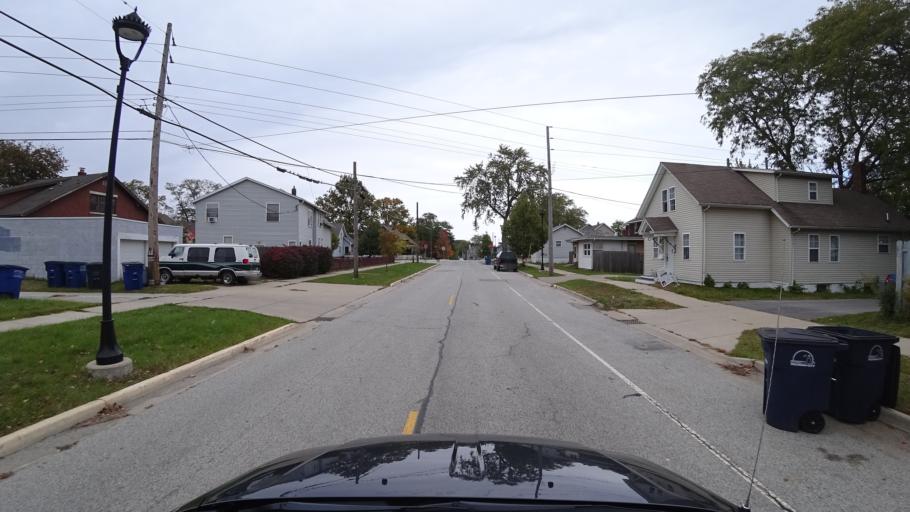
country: US
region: Indiana
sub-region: LaPorte County
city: Michigan City
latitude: 41.7140
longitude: -86.8938
